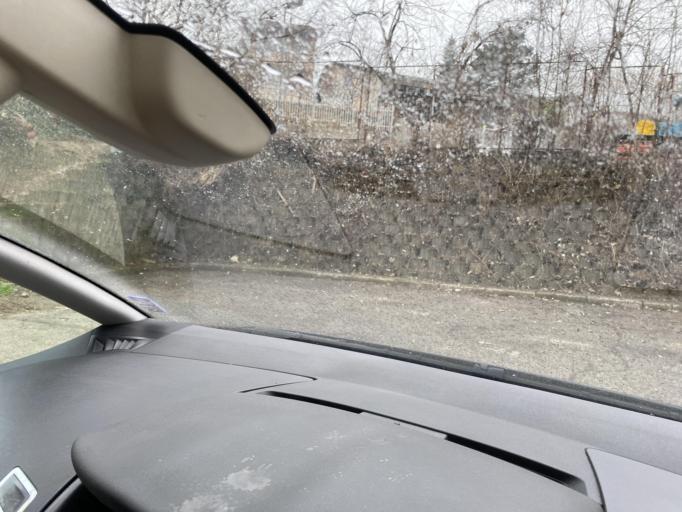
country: MK
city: Radishani
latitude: 42.0580
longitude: 21.4502
